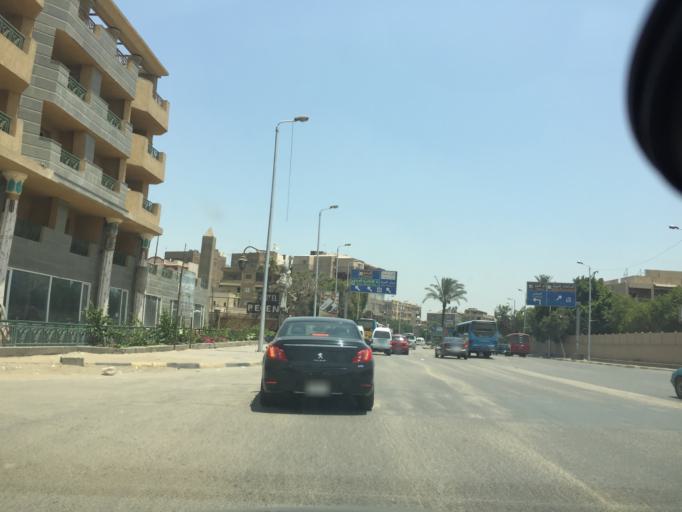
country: EG
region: Al Jizah
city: Al Jizah
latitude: 29.9875
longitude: 31.1322
